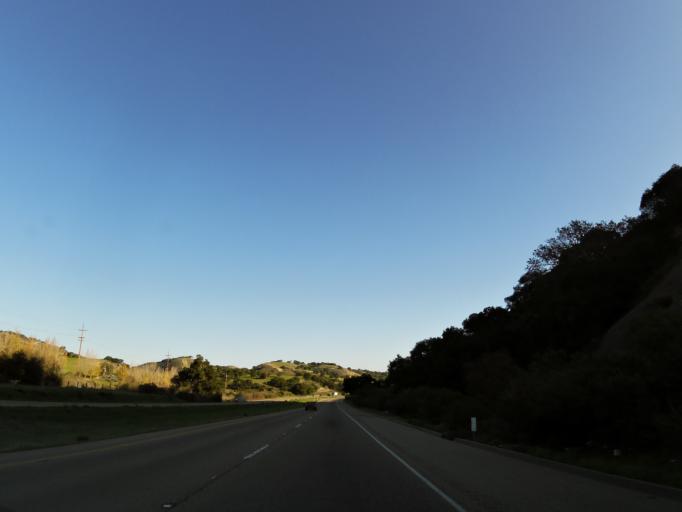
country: US
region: California
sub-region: Santa Barbara County
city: Buellton
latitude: 34.6600
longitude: -120.1787
